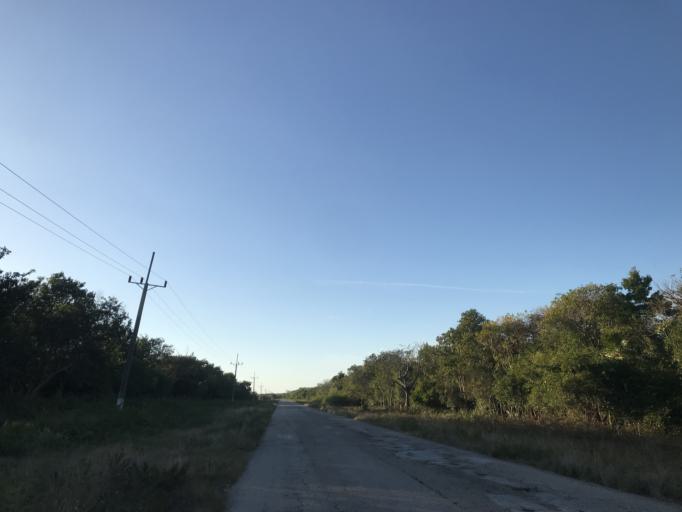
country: CU
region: Cienfuegos
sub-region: Municipio de Aguada de Pasajeros
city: Aguada de Pasajeros
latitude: 22.0779
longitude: -81.0667
